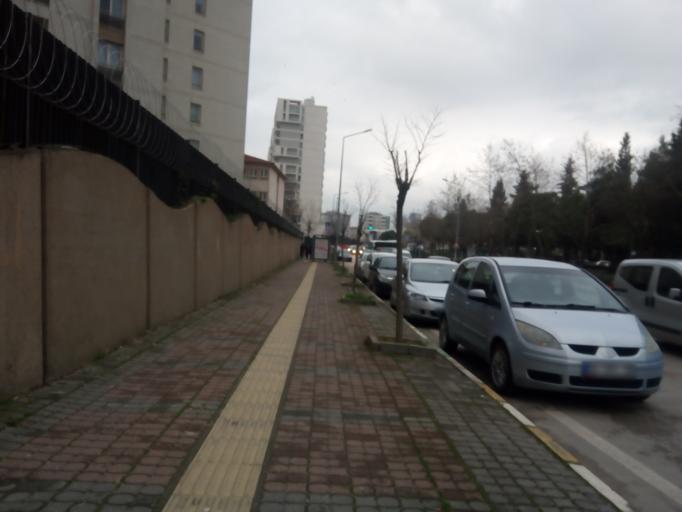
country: TR
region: Bursa
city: Niluefer
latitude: 40.2514
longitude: 28.9614
